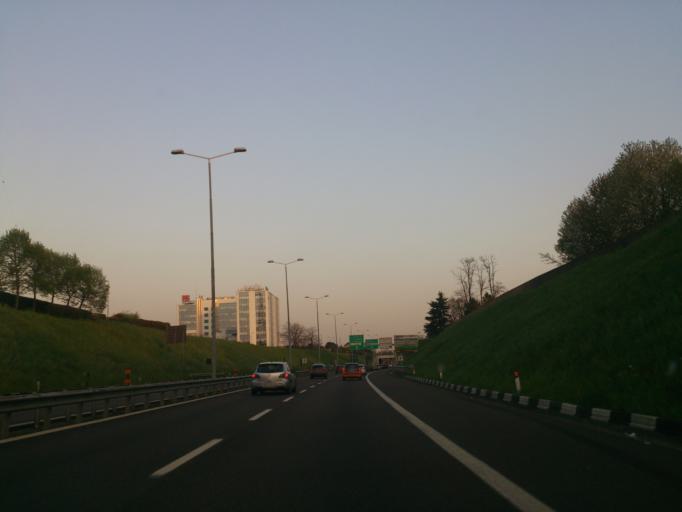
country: IT
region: Lombardy
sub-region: Citta metropolitana di Milano
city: Cinisello Balsamo
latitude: 45.5641
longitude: 9.2344
